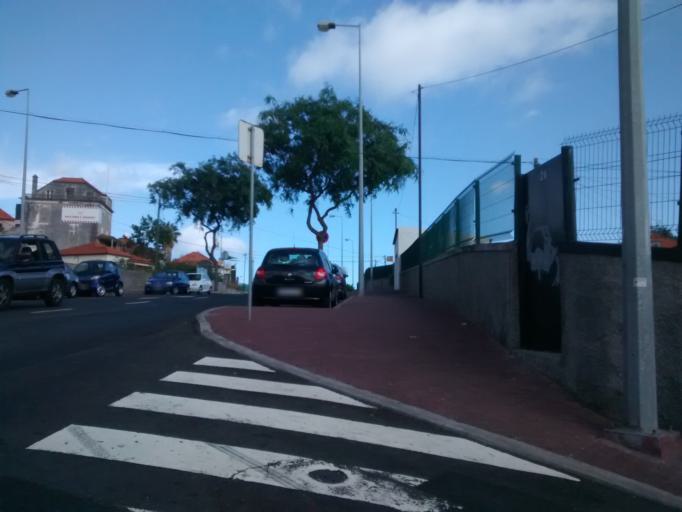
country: PT
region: Madeira
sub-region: Funchal
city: Funchal
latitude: 32.6494
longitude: -16.8967
